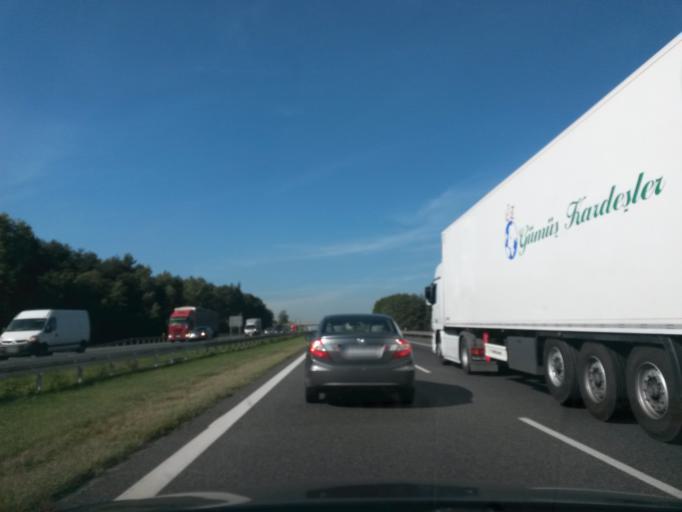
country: PL
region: Silesian Voivodeship
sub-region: Powiat bierunsko-ledzinski
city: Imielin
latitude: 50.1601
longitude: 19.2279
